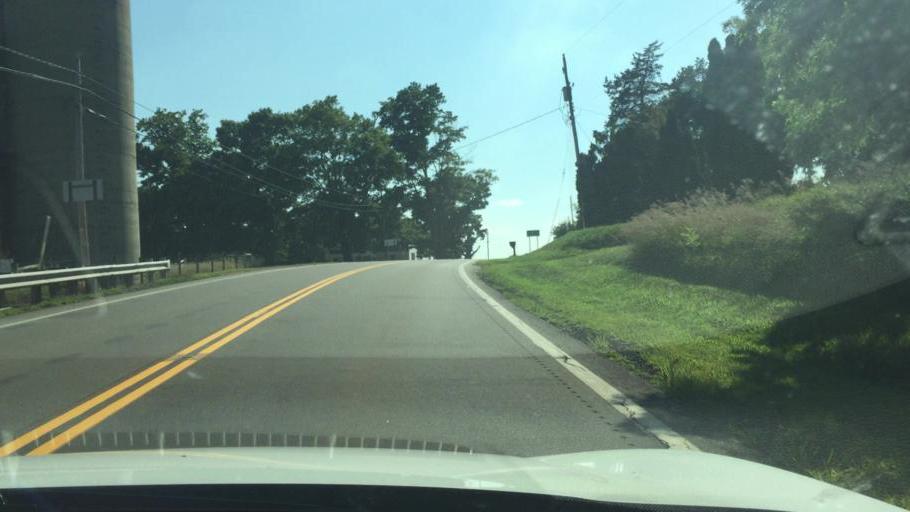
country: US
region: Ohio
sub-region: Clark County
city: Northridge
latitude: 40.0194
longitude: -83.6724
